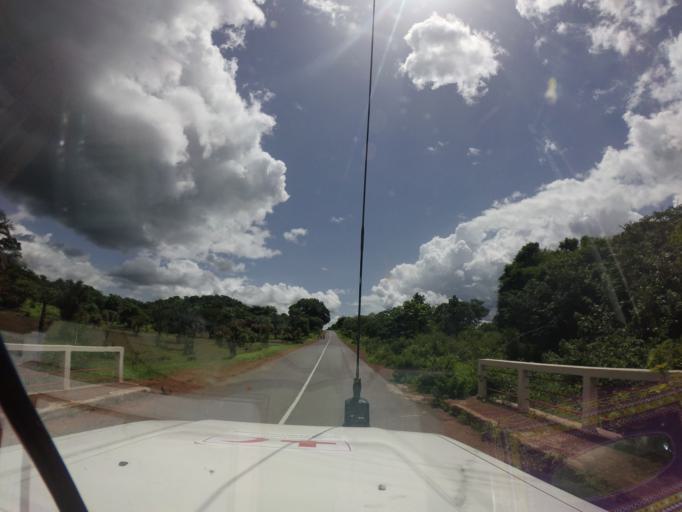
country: SL
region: Northern Province
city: Bindi
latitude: 10.1456
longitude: -11.5852
